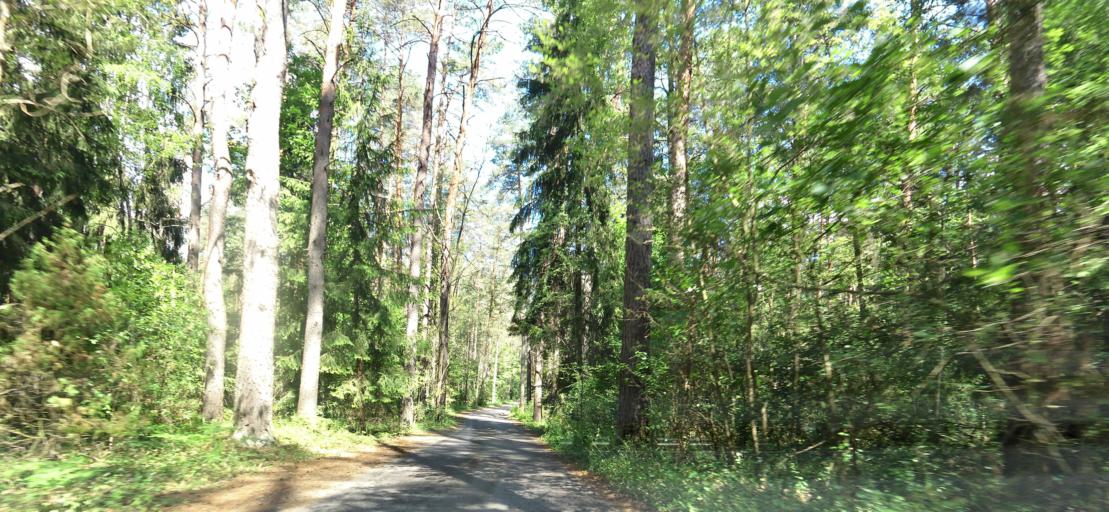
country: LT
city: Nemencine
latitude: 54.8101
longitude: 25.3939
